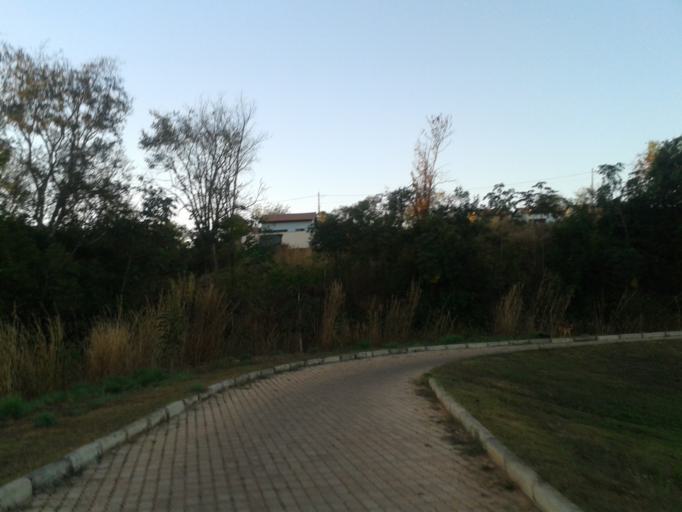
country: BR
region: Goias
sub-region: Sao Miguel Do Araguaia
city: Sao Miguel do Araguaia
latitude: -13.2685
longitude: -50.1669
